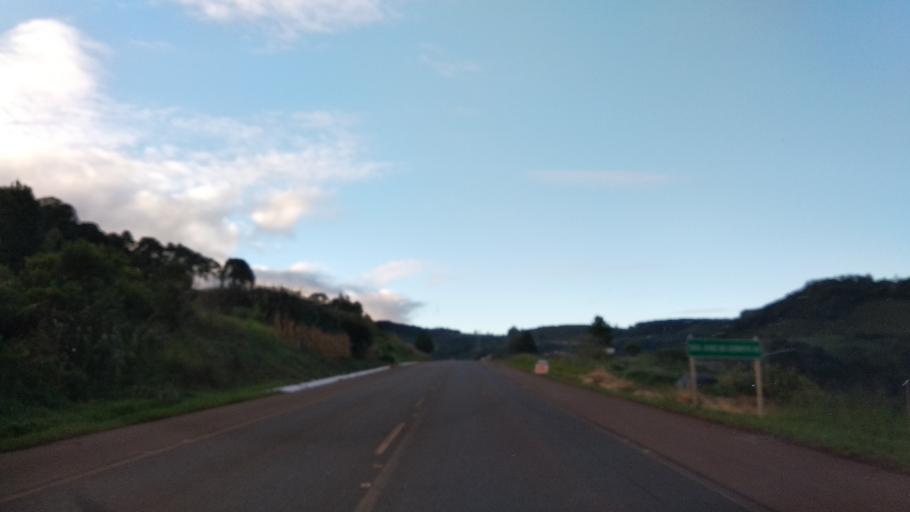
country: BR
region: Santa Catarina
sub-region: Curitibanos
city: Curitibanos
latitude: -27.5555
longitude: -50.8435
